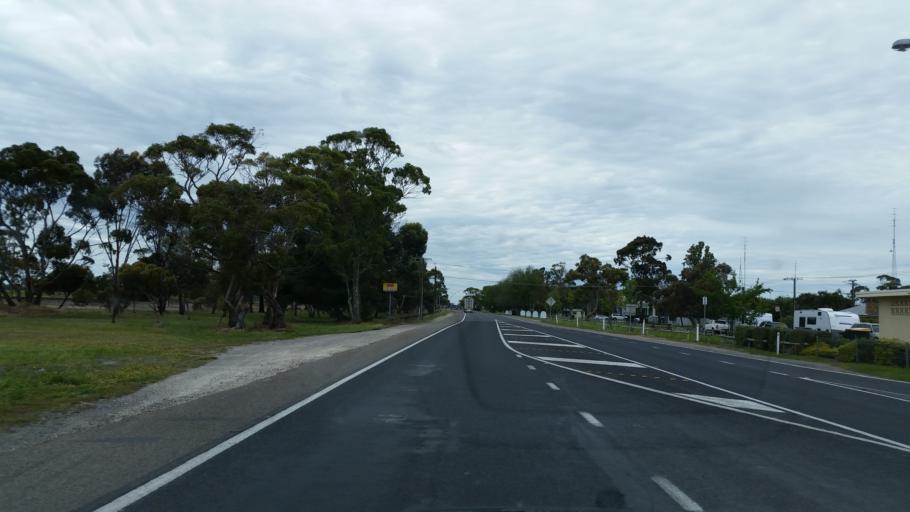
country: AU
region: South Australia
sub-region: Tatiara
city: Keith
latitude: -36.0979
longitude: 140.3550
